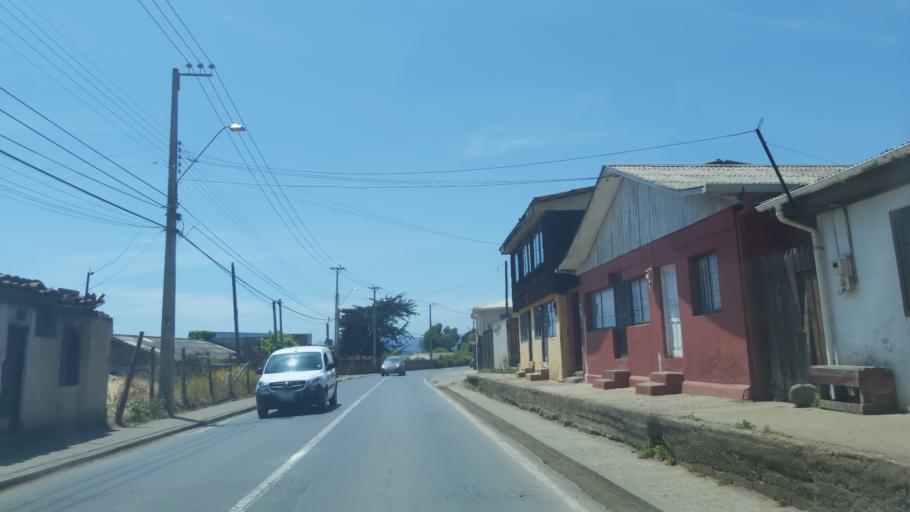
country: CL
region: Maule
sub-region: Provincia de Cauquenes
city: Cauquenes
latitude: -35.8164
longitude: -72.5839
